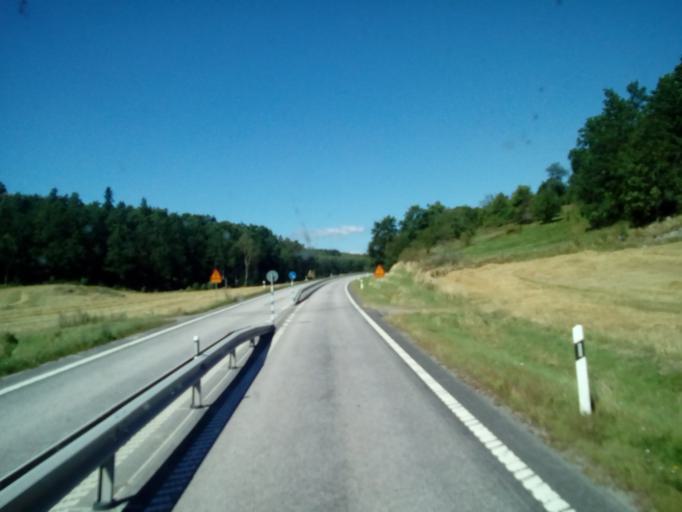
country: SE
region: OEstergoetland
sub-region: Kinda Kommun
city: Kisa
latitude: 58.0601
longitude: 15.6599
